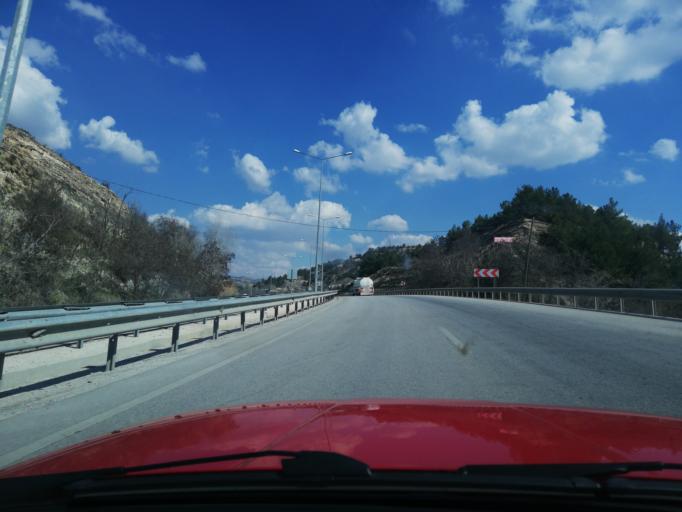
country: TR
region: Burdur
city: Burdur
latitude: 37.6979
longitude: 30.3288
